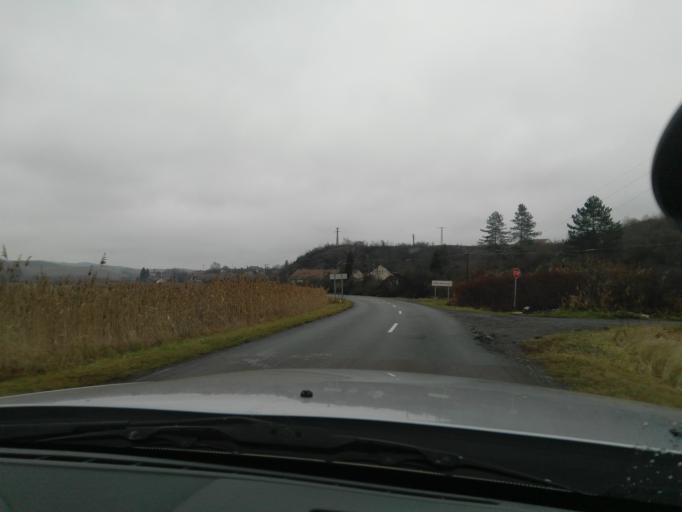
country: HU
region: Nograd
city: Matraterenye
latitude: 48.0414
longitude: 19.9237
